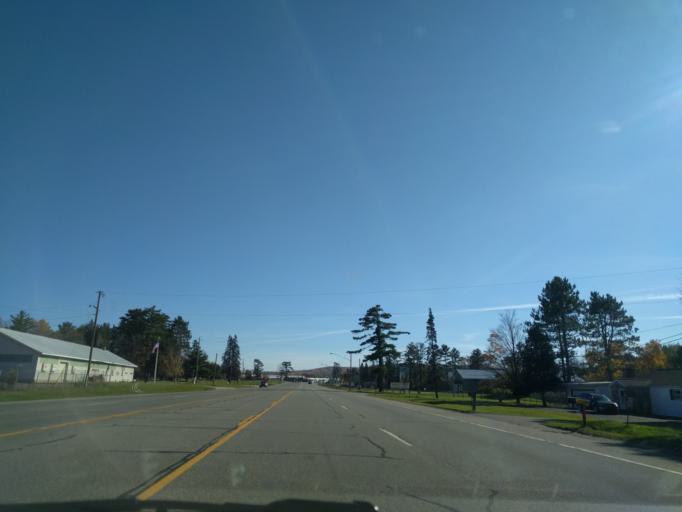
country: US
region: Michigan
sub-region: Dickinson County
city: Iron Mountain
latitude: 45.8500
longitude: -88.0524
